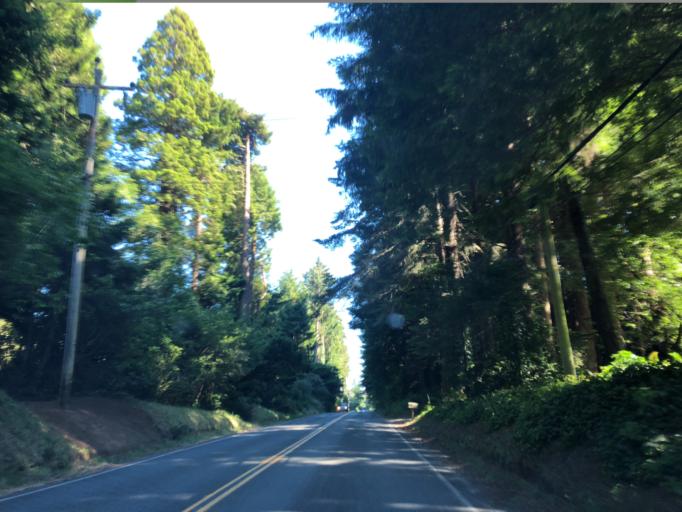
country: US
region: California
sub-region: Humboldt County
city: Westhaven-Moonstone
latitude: 41.0713
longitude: -124.1440
